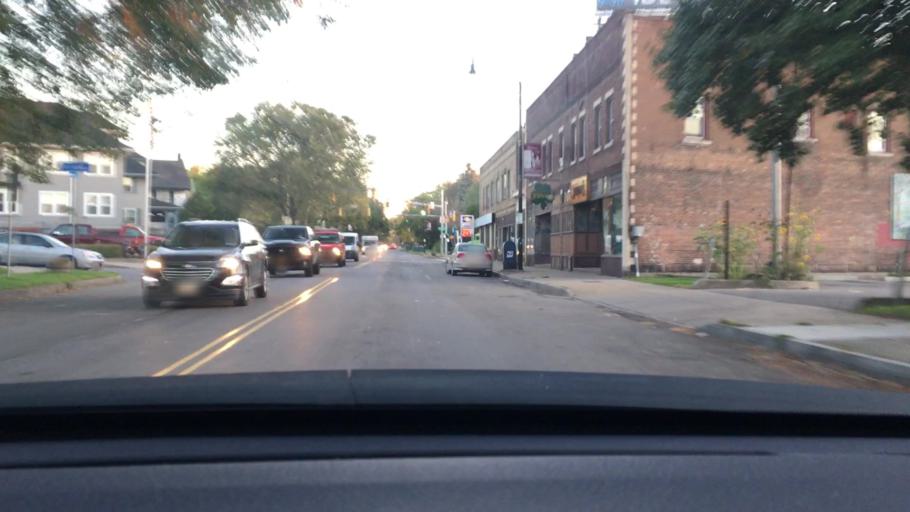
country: US
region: New York
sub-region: Monroe County
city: Brighton
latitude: 43.1704
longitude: -77.5605
